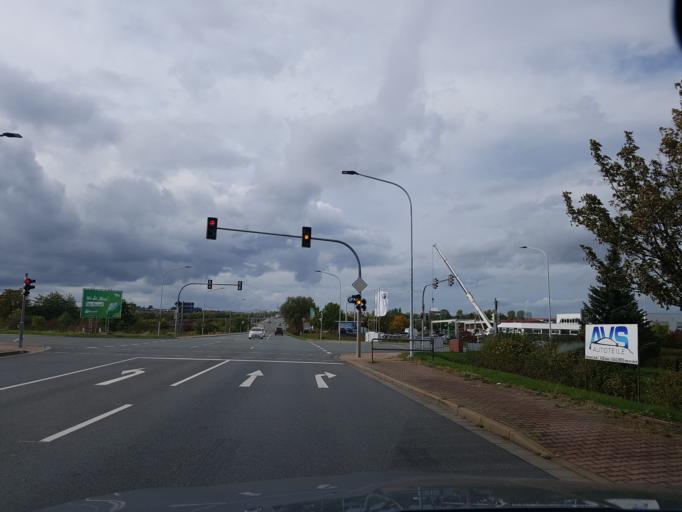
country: DE
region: Saxony
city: Riesa
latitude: 51.2946
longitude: 13.2863
